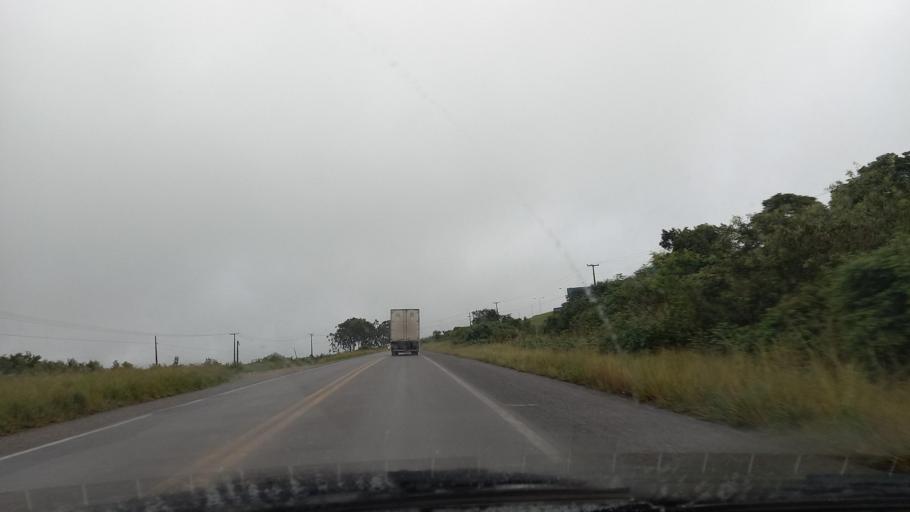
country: BR
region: Pernambuco
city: Garanhuns
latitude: -8.8746
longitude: -36.5279
